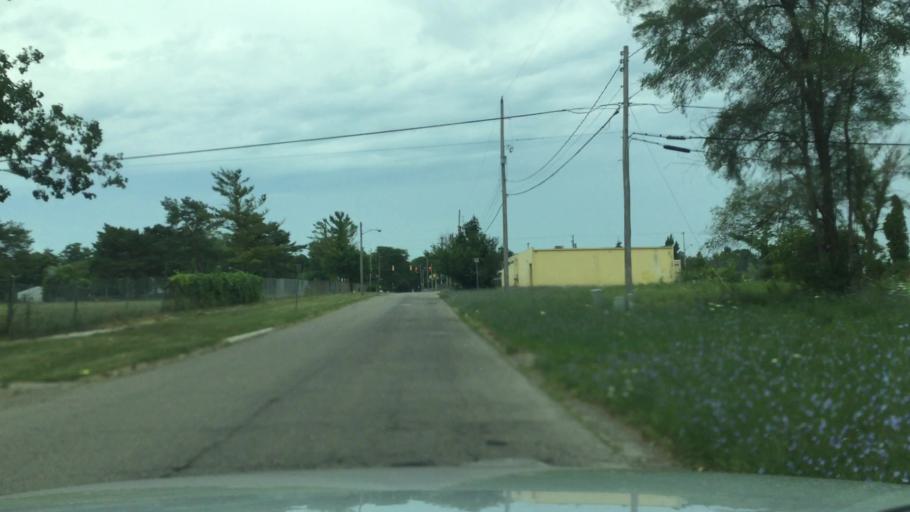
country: US
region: Michigan
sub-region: Genesee County
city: Beecher
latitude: 43.0627
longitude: -83.7296
